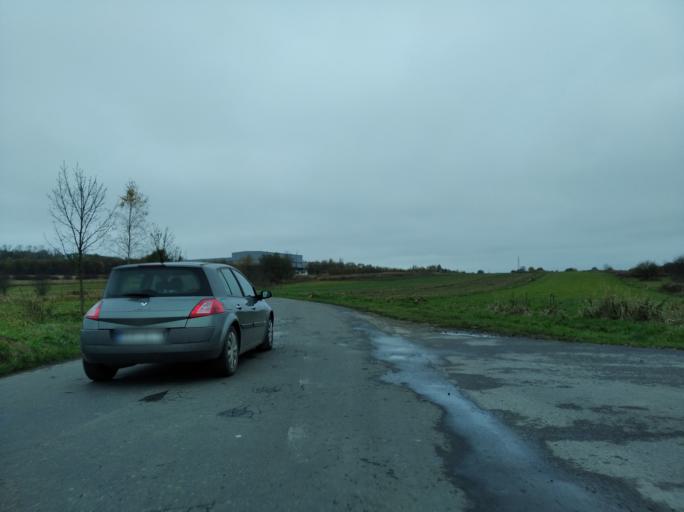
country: PL
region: Subcarpathian Voivodeship
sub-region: Krosno
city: Krosno
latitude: 49.7168
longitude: 21.7597
